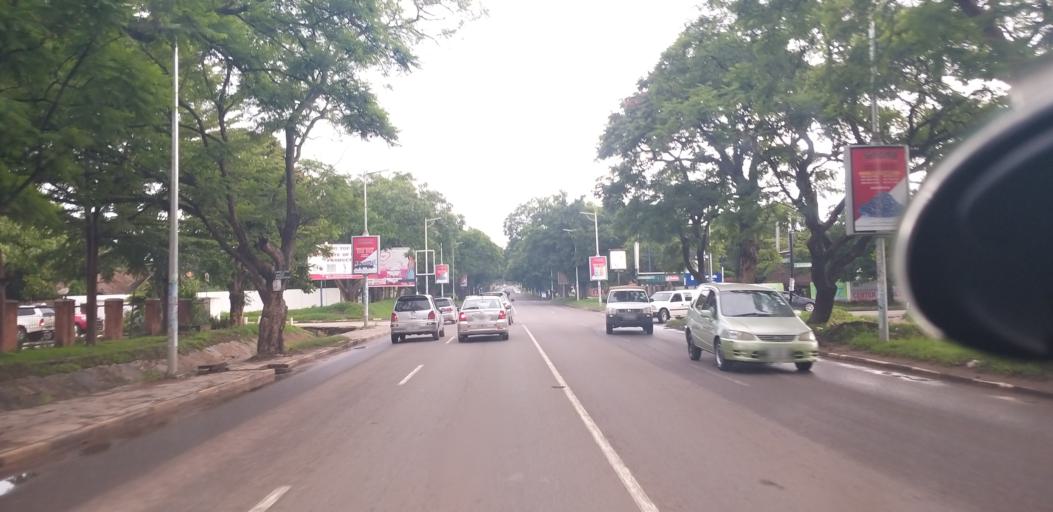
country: ZM
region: Lusaka
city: Lusaka
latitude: -15.4151
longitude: 28.2918
